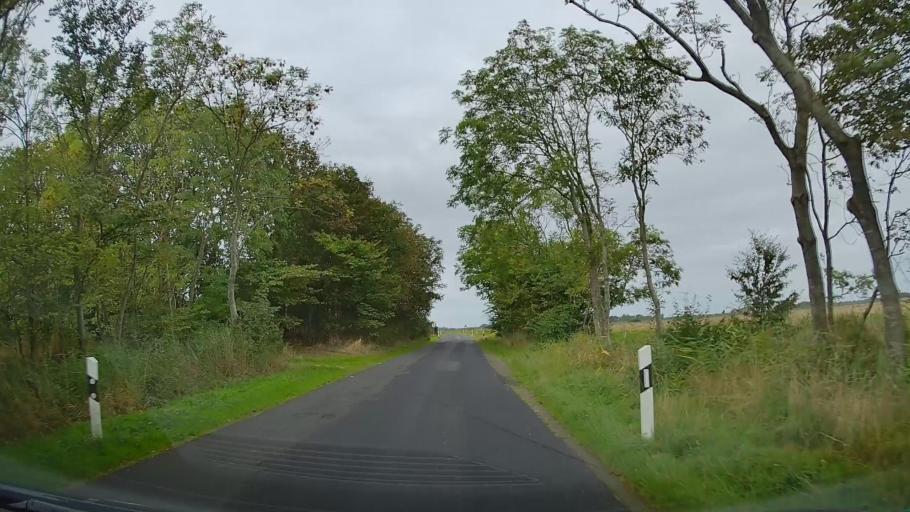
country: DE
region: Schleswig-Holstein
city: Emmelsbull-Horsbull
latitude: 54.8106
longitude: 8.6824
